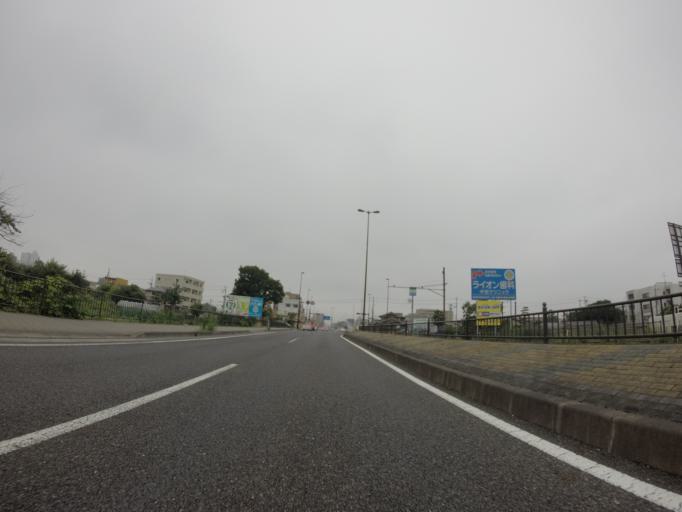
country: JP
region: Shizuoka
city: Shizuoka-shi
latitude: 34.9605
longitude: 138.3910
